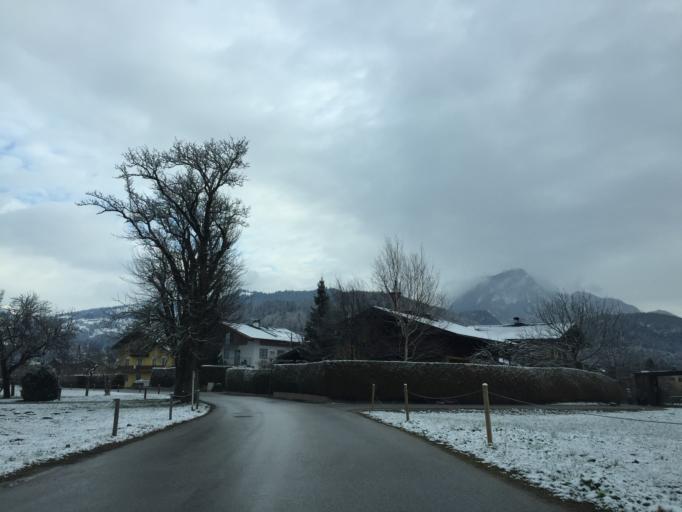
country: AT
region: Salzburg
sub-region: Politischer Bezirk Hallein
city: Golling an der Salzach
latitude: 47.5942
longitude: 13.1622
